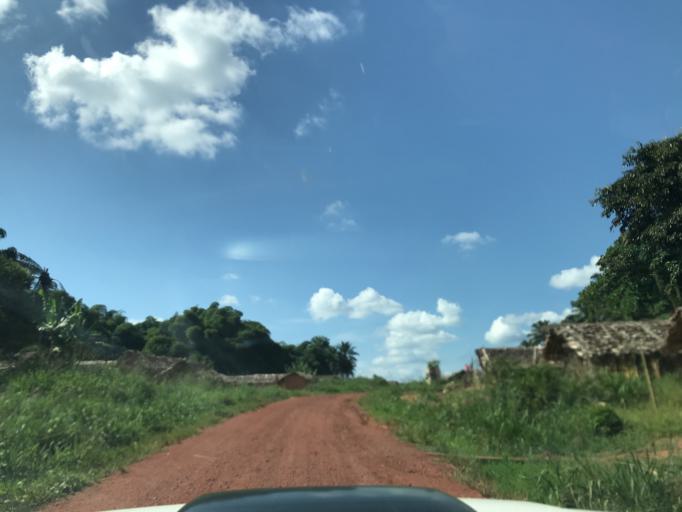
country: CD
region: Eastern Province
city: Kisangani
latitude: 1.2478
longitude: 25.2731
